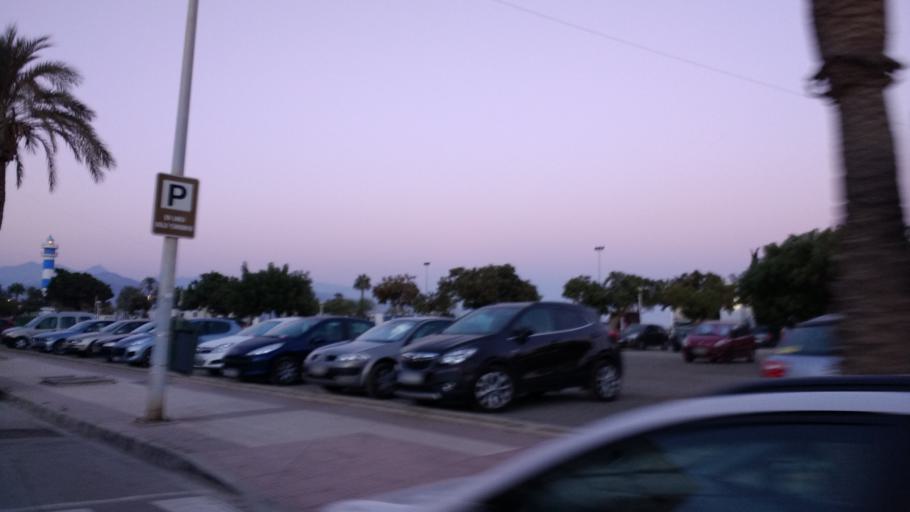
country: ES
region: Andalusia
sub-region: Provincia de Malaga
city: Velez-Malaga
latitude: 36.7335
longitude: -4.0983
